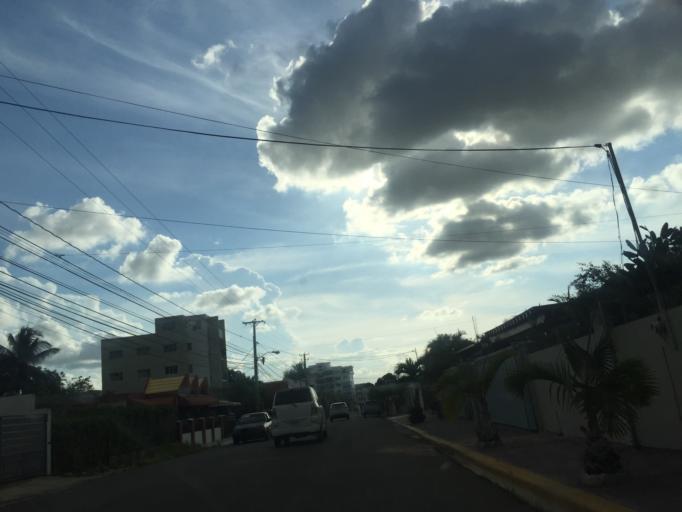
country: DO
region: Santiago
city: Santiago de los Caballeros
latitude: 19.4346
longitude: -70.6643
